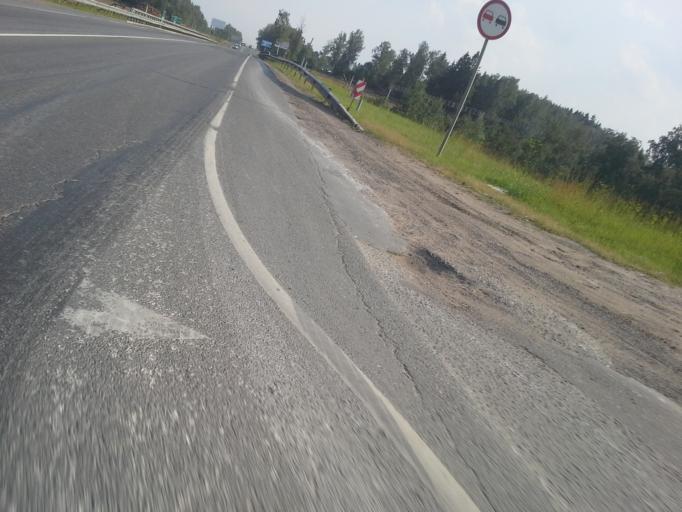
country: RU
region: Moskovskaya
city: Istra
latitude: 55.8951
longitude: 36.9444
